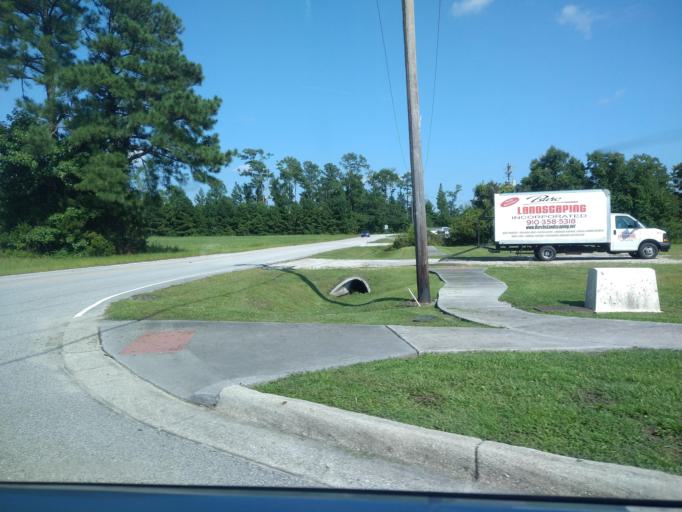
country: US
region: North Carolina
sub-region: Onslow County
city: Piney Green
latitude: 34.7413
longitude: -77.3627
